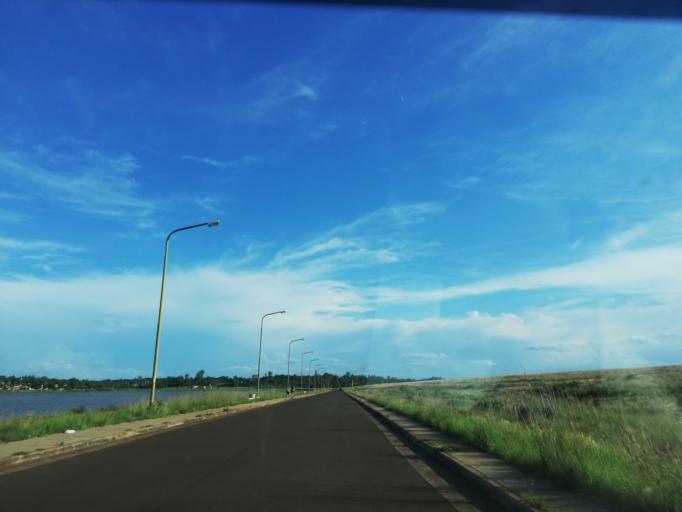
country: AR
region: Misiones
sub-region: Departamento de Capital
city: Posadas
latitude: -27.3861
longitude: -55.9560
